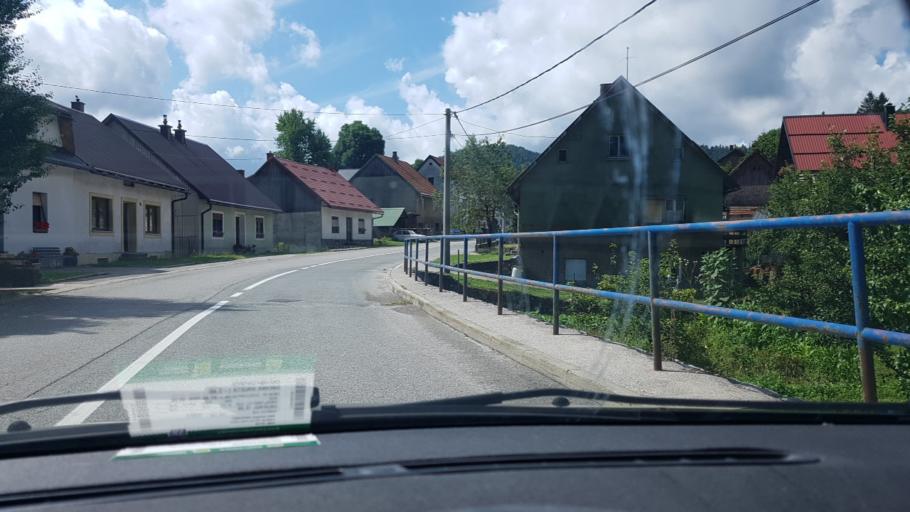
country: HR
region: Primorsko-Goranska
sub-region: Grad Delnice
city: Delnice
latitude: 45.3612
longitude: 14.7535
